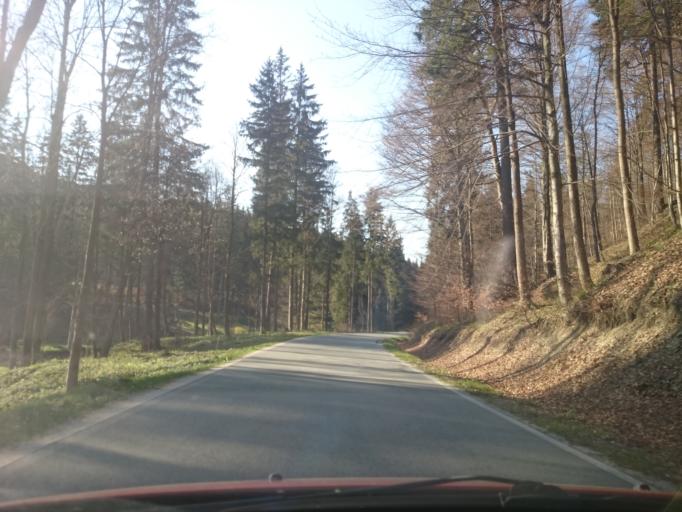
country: PL
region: Lower Silesian Voivodeship
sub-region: Powiat klodzki
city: Duszniki-Zdroj
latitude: 50.3572
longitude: 16.3957
